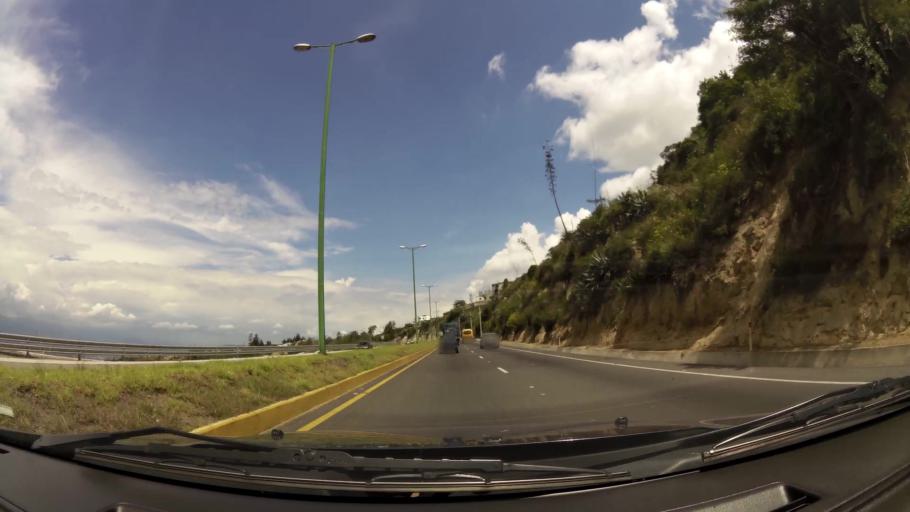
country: EC
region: Pichincha
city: Quito
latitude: -0.0969
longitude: -78.4183
